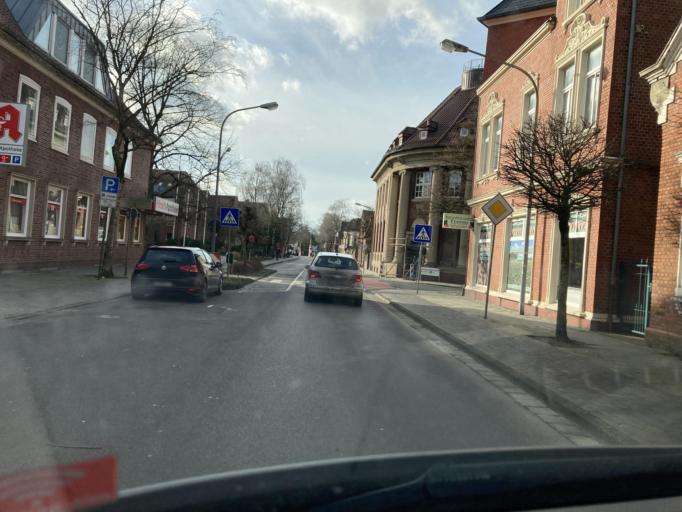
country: DE
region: Lower Saxony
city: Leer
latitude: 53.2336
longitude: 7.4573
